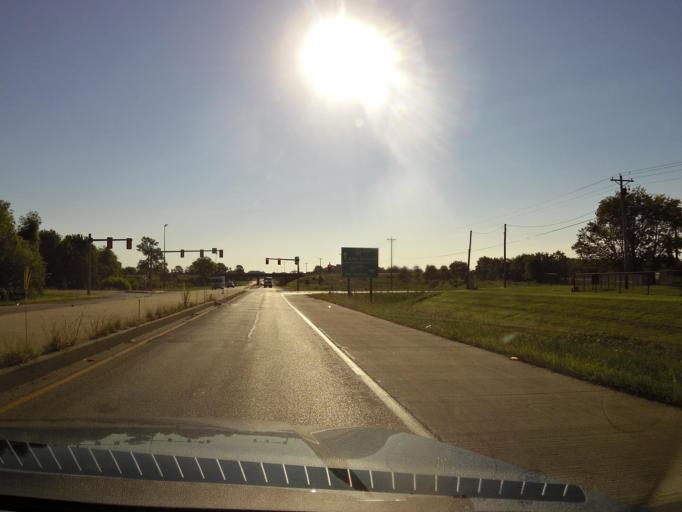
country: US
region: Illinois
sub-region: Clinton County
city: New Baden
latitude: 38.5355
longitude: -89.7325
